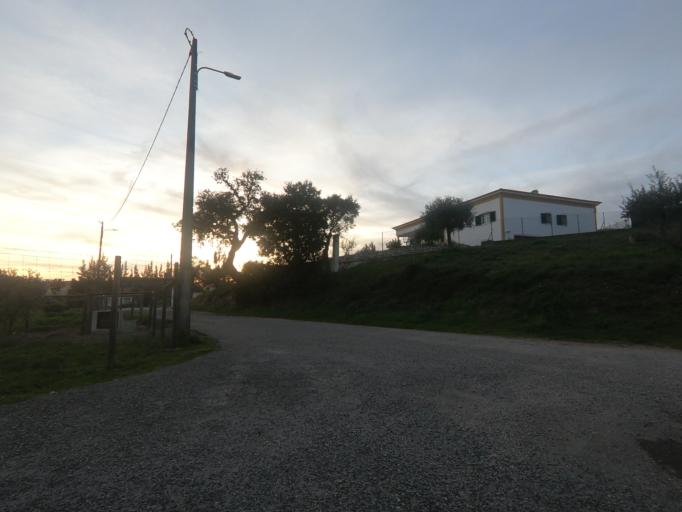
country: PT
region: Setubal
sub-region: Setubal
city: Setubal
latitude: 38.5254
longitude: -8.8377
